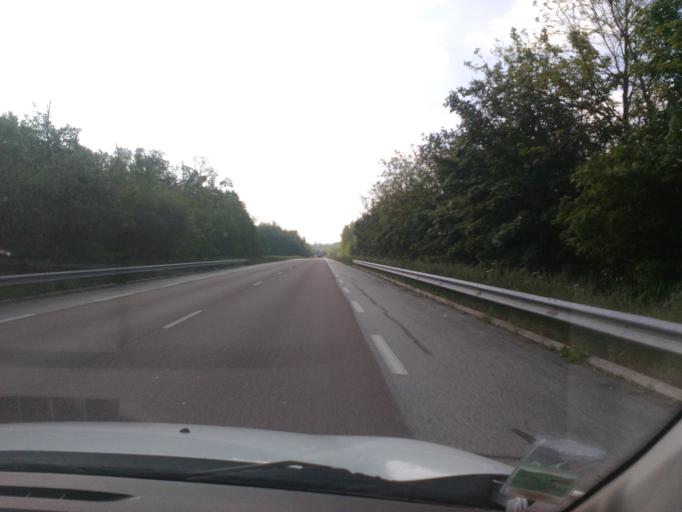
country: FR
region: Lorraine
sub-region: Departement des Vosges
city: Uxegney
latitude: 48.2016
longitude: 6.3927
